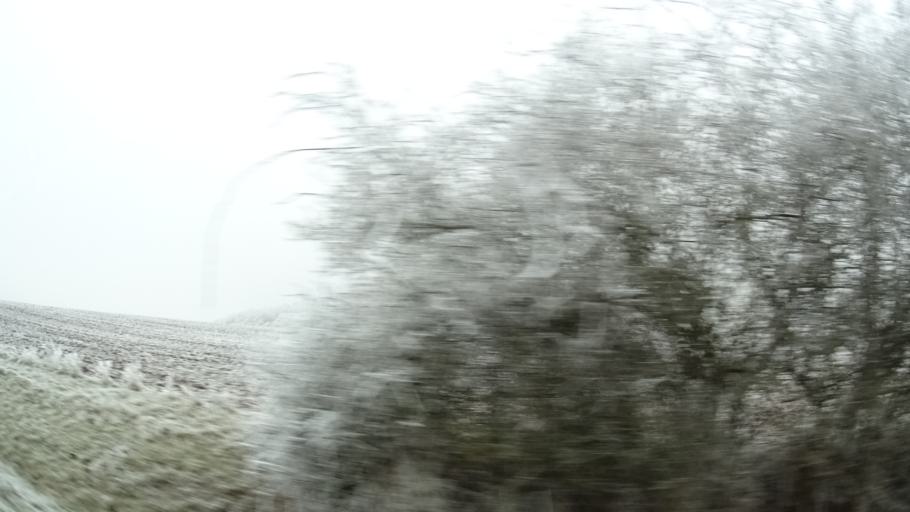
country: DE
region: Thuringia
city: Henneberg
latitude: 50.5199
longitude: 10.3392
